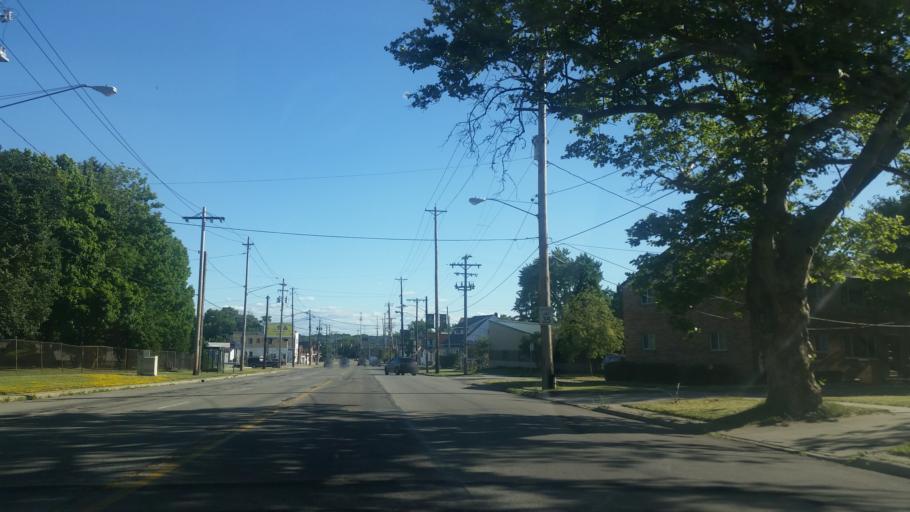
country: US
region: Ohio
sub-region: Cuyahoga County
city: Brooklyn Heights
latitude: 41.4287
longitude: -81.7084
